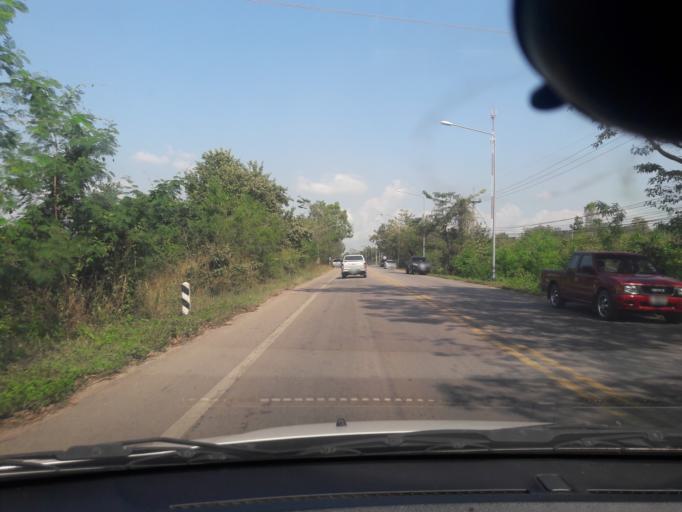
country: TH
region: Lampang
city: Lampang
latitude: 18.2246
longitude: 99.4905
